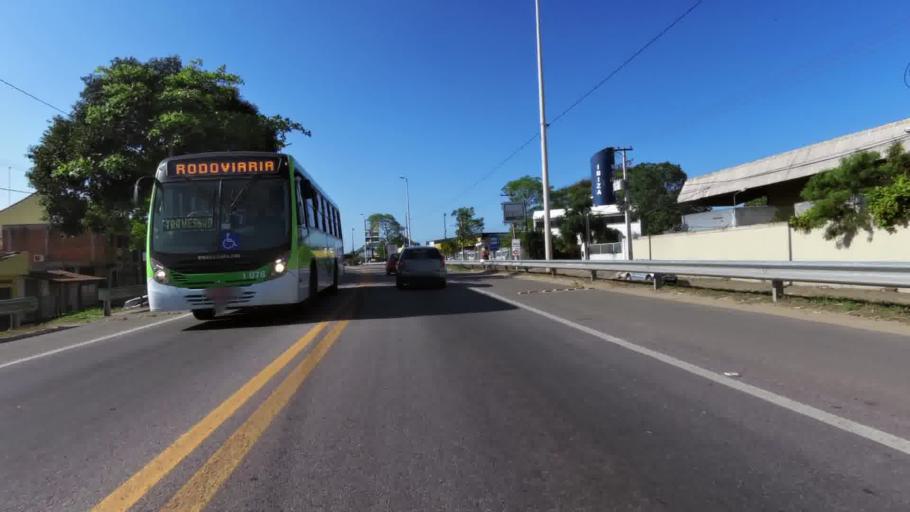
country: BR
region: Rio de Janeiro
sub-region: Campos Dos Goytacazes
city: Campos
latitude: -21.7152
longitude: -41.3093
